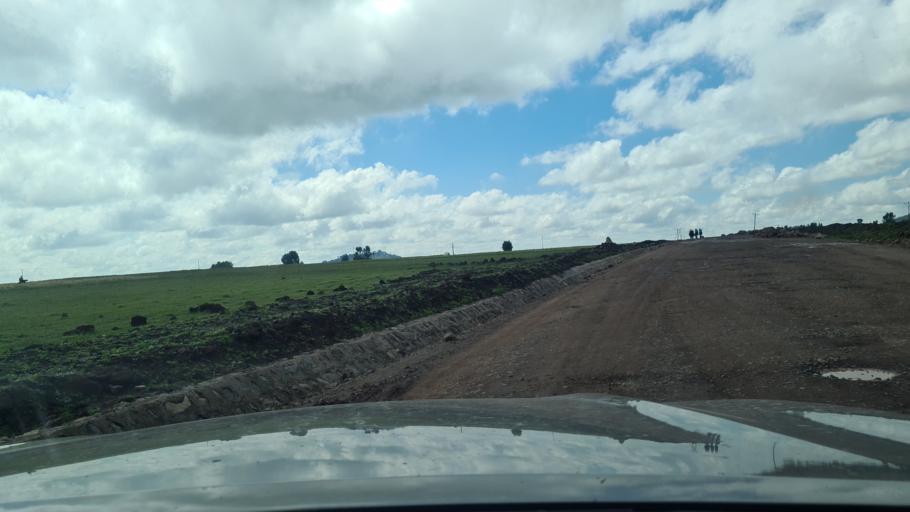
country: ET
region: Oromiya
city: Huruta
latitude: 8.0940
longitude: 39.5359
